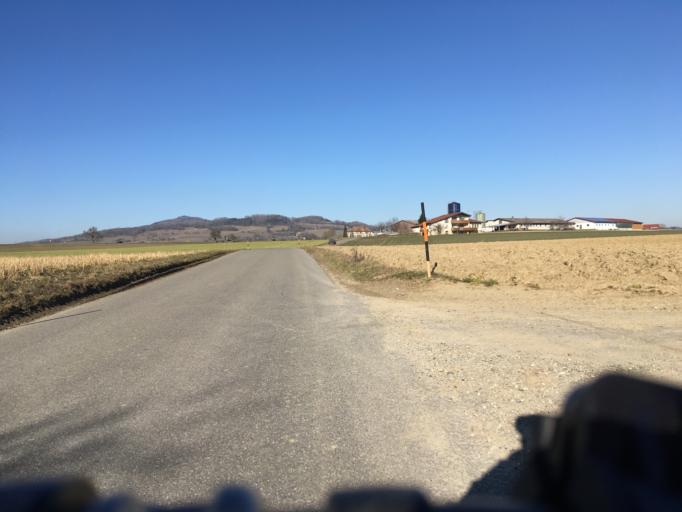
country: DE
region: Baden-Wuerttemberg
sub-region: Freiburg Region
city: Gottmadingen
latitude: 47.7474
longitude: 8.7445
